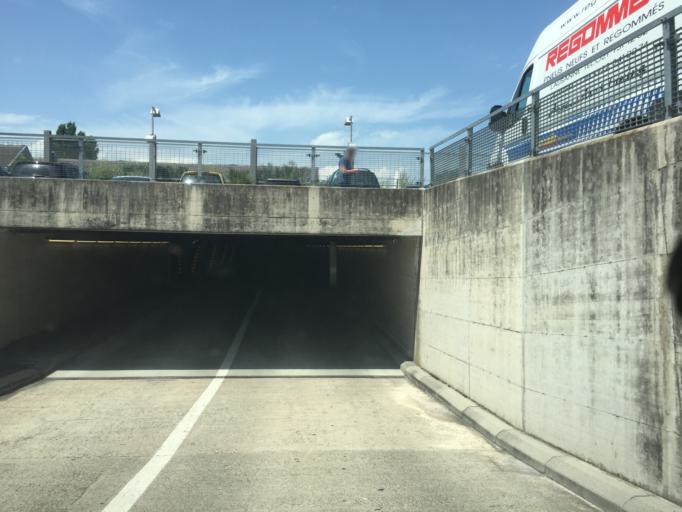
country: CH
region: Vaud
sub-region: Ouest Lausannois District
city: Crissier
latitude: 46.5471
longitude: 6.5644
